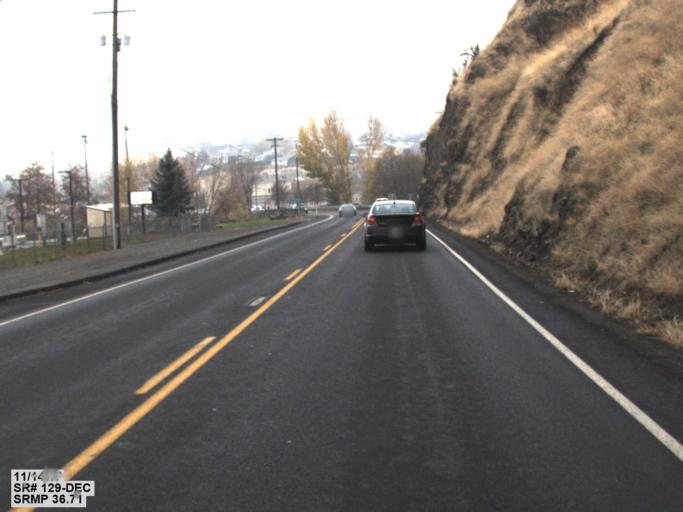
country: US
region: Washington
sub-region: Asotin County
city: Asotin
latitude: 46.3425
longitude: -117.0568
